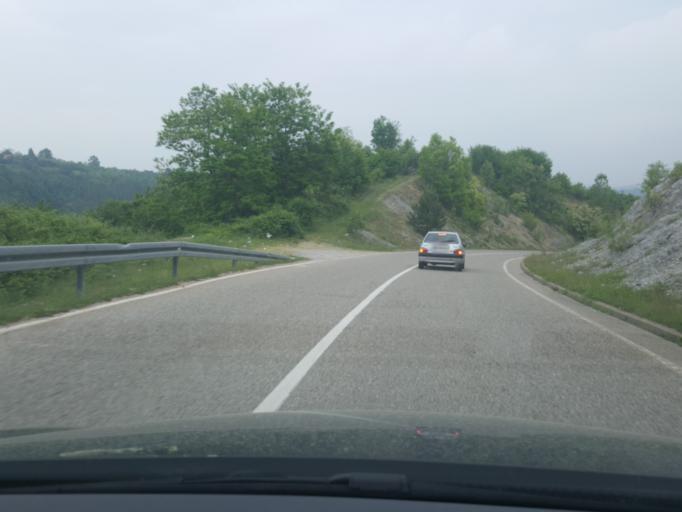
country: RS
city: Kamenica
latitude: 44.2534
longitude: 19.7526
